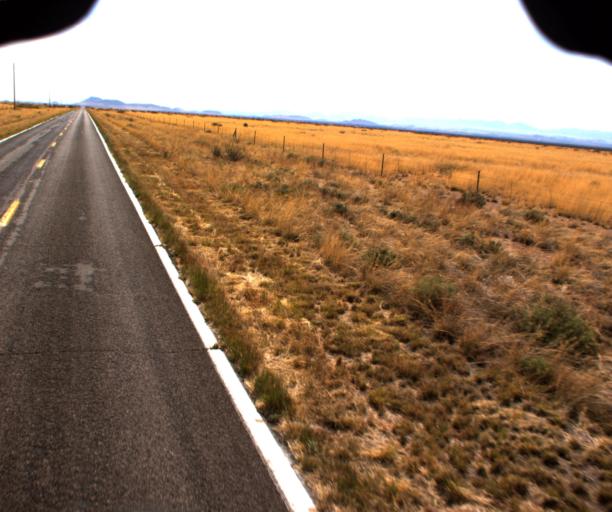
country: US
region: Arizona
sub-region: Cochise County
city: Willcox
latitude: 31.9467
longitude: -109.4806
